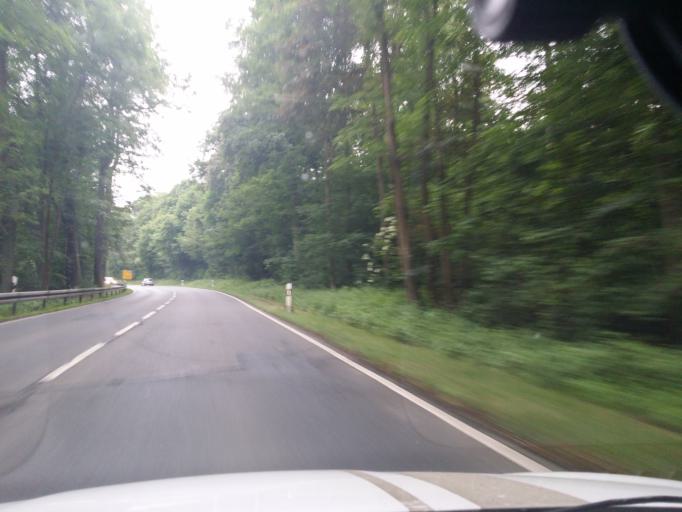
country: DE
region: Hesse
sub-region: Regierungsbezirk Darmstadt
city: Hofheim am Taunus
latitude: 50.0936
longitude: 8.4282
